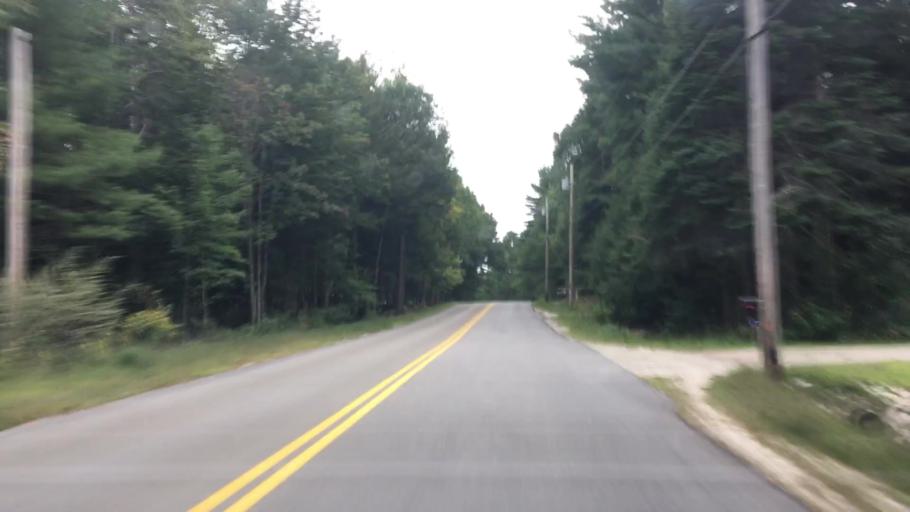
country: US
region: Maine
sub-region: Cumberland County
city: New Gloucester
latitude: 43.9103
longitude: -70.2399
